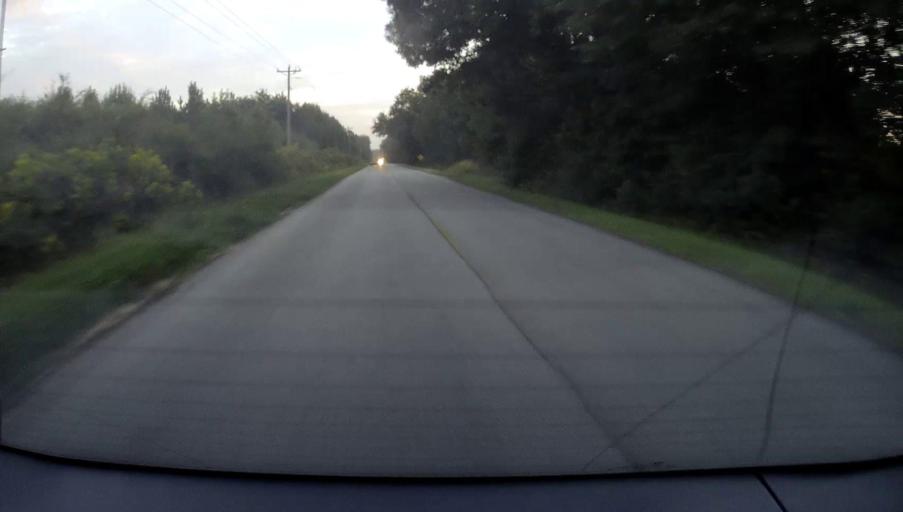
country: US
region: Georgia
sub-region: Butts County
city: Jackson
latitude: 33.2882
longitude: -84.0432
